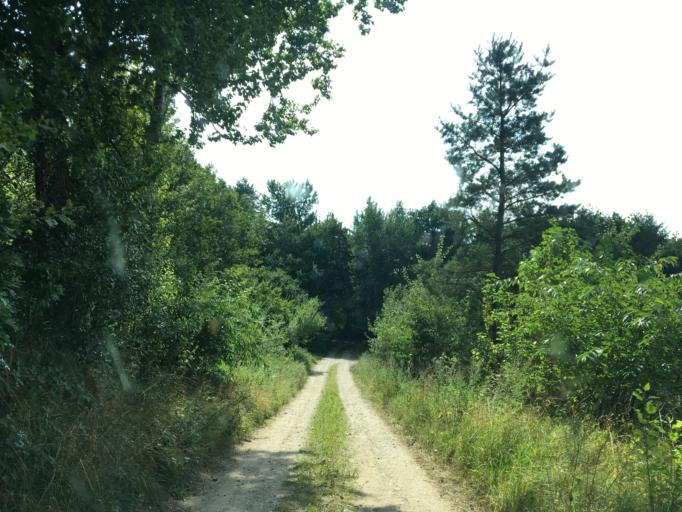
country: DK
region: South Denmark
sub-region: Middelfart Kommune
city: Ejby
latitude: 55.3900
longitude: 9.9477
